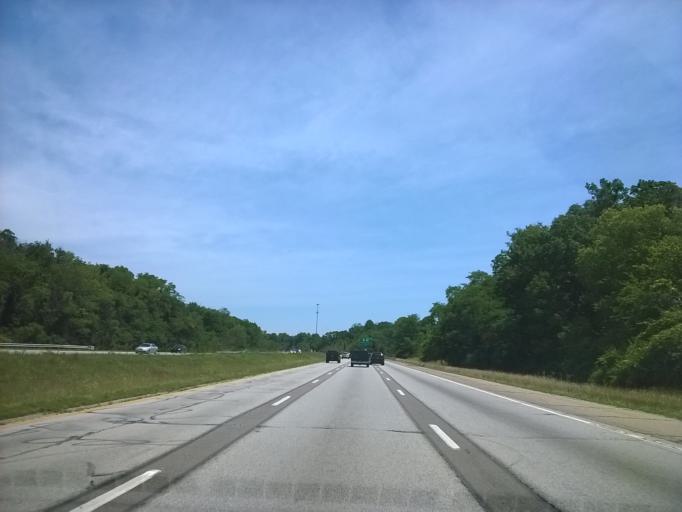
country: US
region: Ohio
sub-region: Hamilton County
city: Dry Ridge
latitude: 39.2421
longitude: -84.6188
